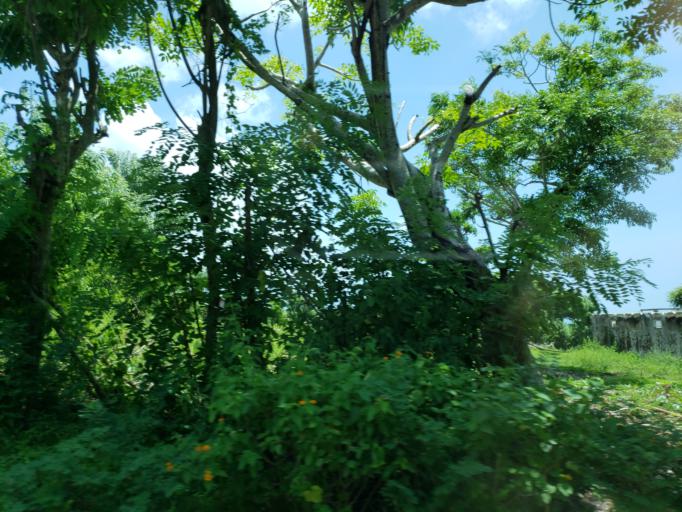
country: ID
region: Bali
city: Kangin
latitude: -8.8429
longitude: 115.1398
